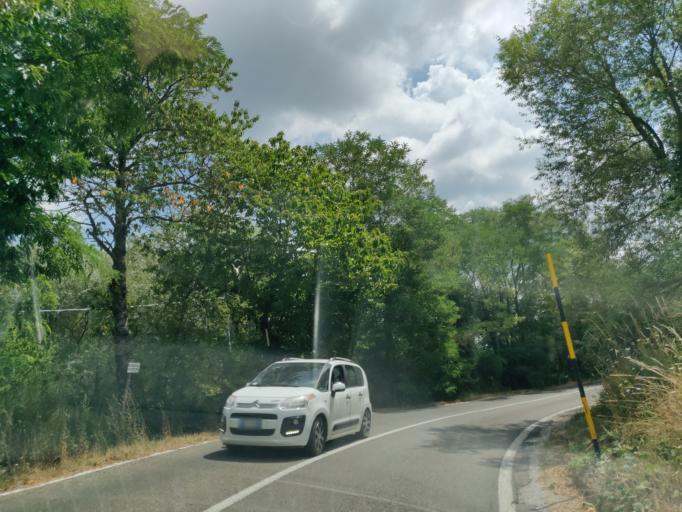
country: IT
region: Tuscany
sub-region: Provincia di Siena
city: Abbadia San Salvatore
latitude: 42.8946
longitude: 11.6572
